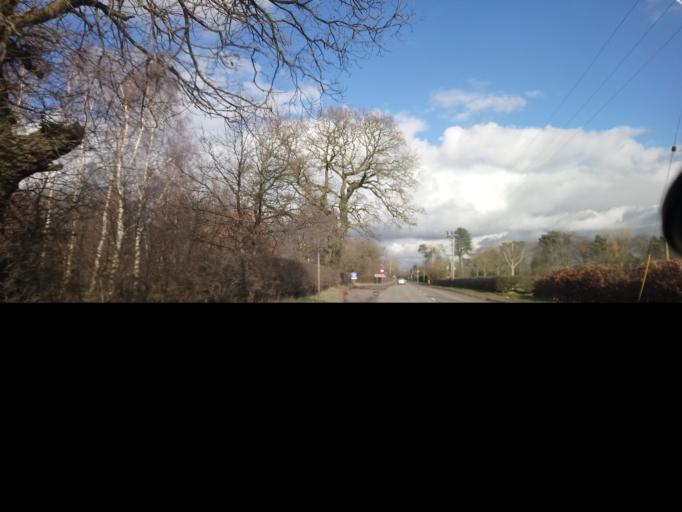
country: GB
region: England
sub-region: Cheshire West and Chester
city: Oakmere
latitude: 53.2035
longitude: -2.6278
